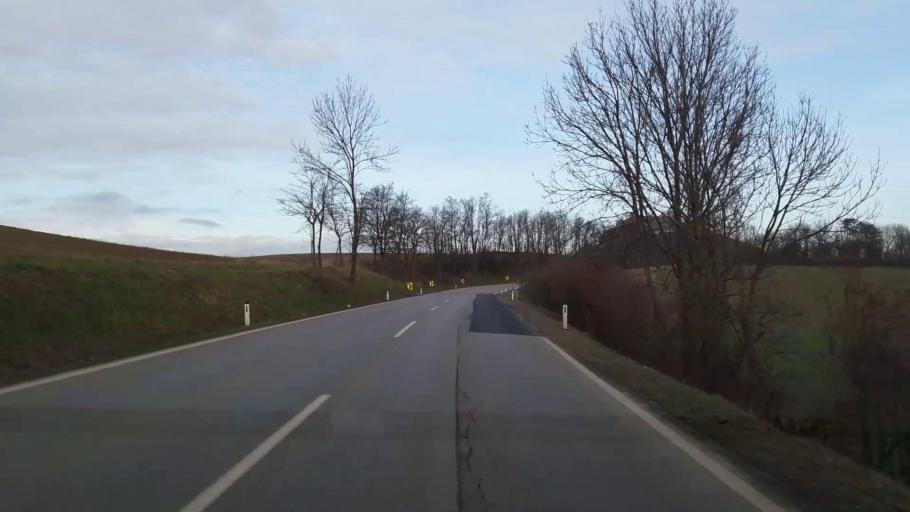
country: AT
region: Lower Austria
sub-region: Politischer Bezirk Mistelbach
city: Staatz
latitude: 48.6680
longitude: 16.4920
